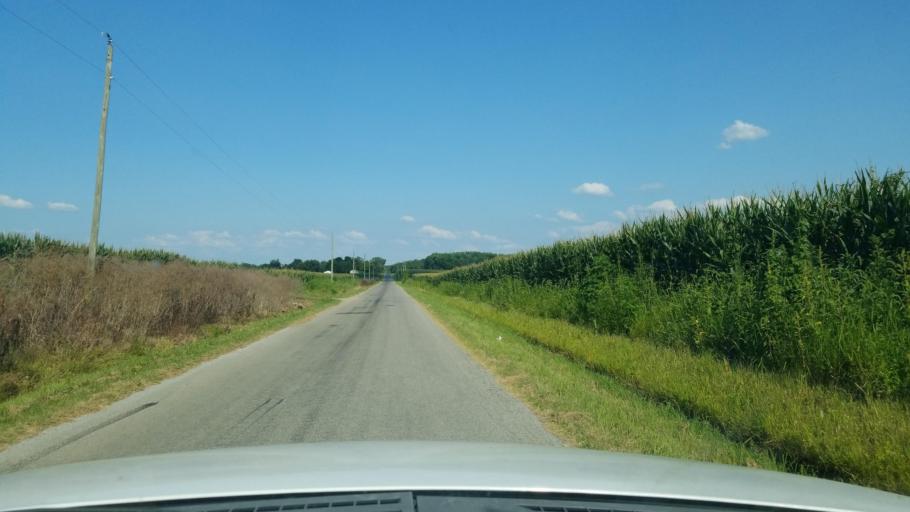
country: US
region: Illinois
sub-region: Saline County
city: Eldorado
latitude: 37.8047
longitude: -88.4784
